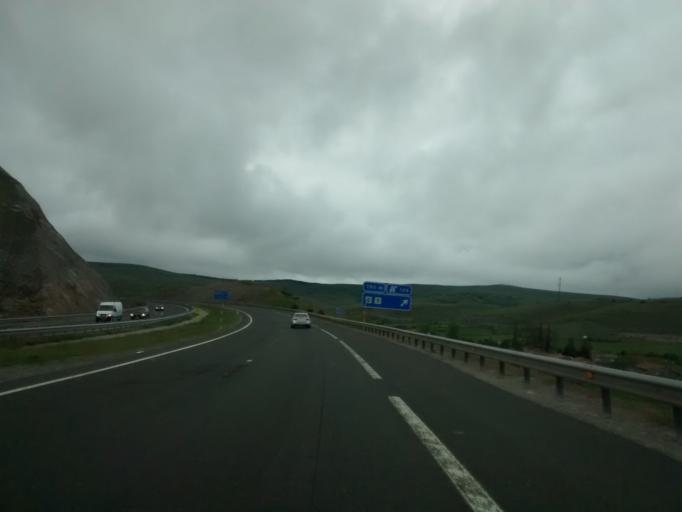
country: ES
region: Cantabria
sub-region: Provincia de Cantabria
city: Villaescusa
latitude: 42.9312
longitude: -4.1223
